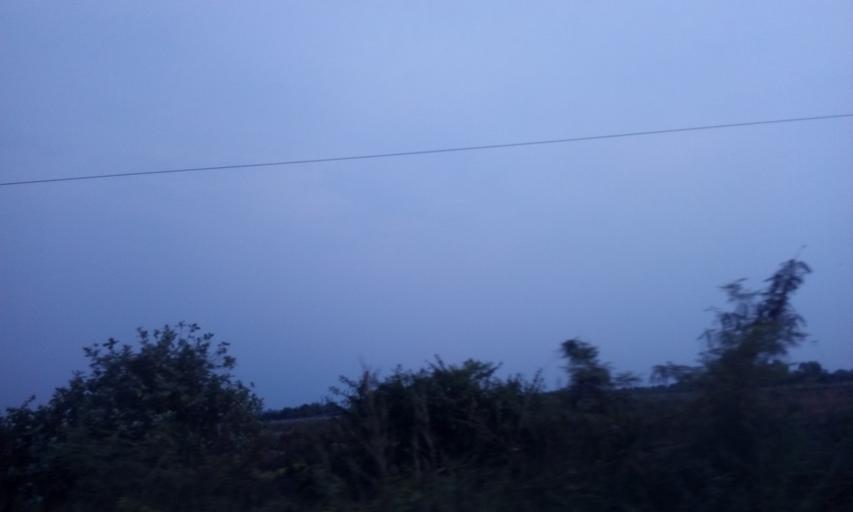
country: TH
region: Chachoengsao
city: Ban Pho
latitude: 13.6036
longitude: 101.1385
